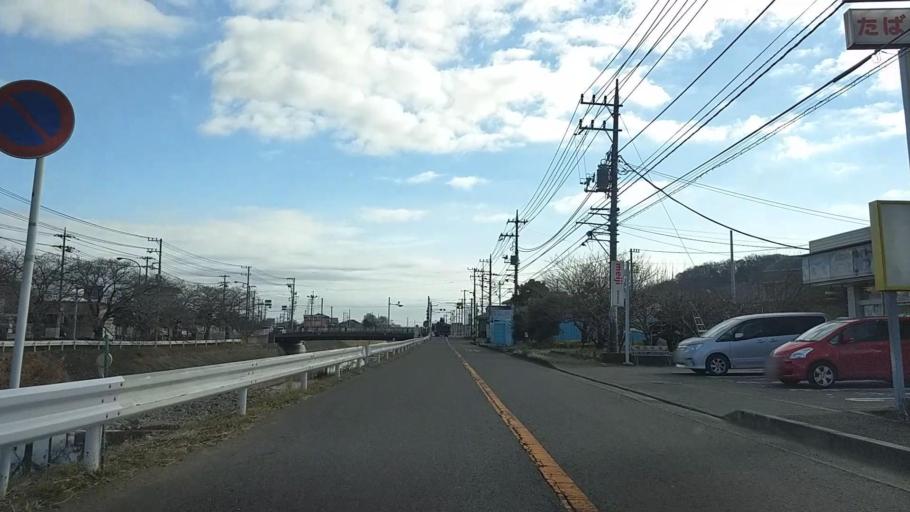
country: JP
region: Kanagawa
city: Isehara
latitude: 35.4348
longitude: 139.3145
